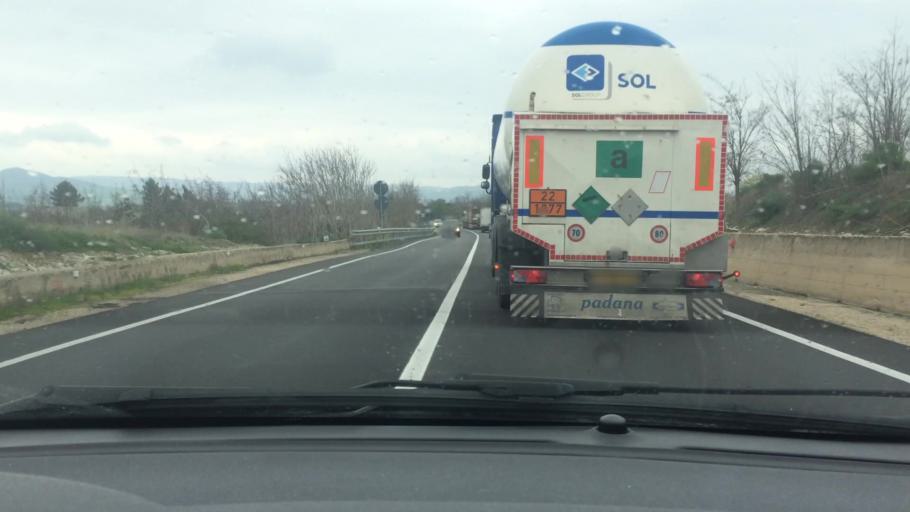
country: IT
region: Basilicate
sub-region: Provincia di Matera
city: Matera
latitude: 40.6165
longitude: 16.5796
